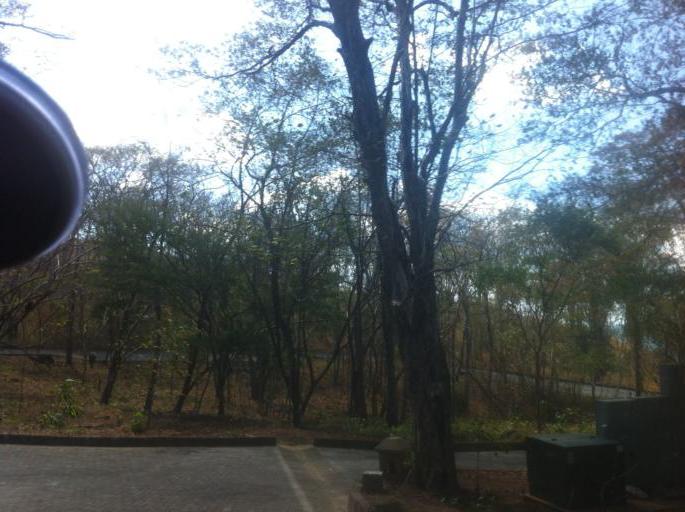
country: NI
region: Rivas
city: Tola
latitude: 11.3794
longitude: -86.0269
